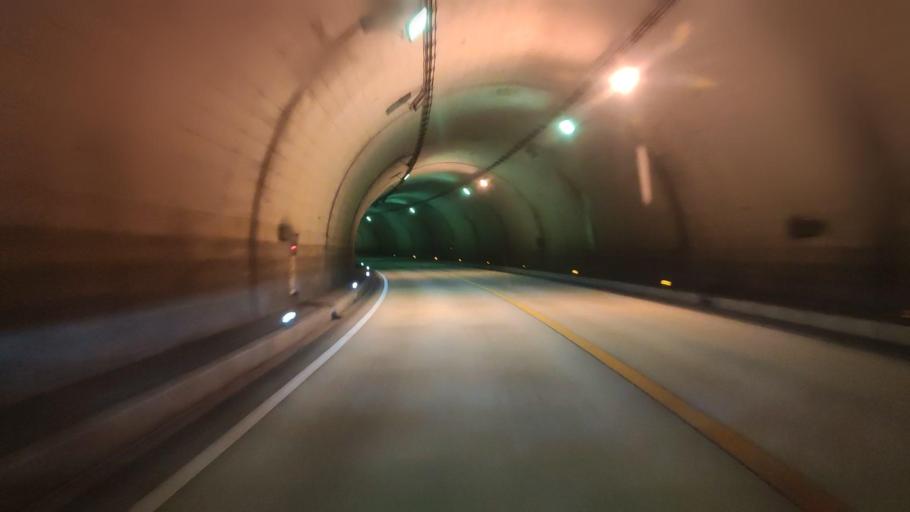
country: JP
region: Wakayama
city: Shingu
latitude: 33.8004
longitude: 135.8855
